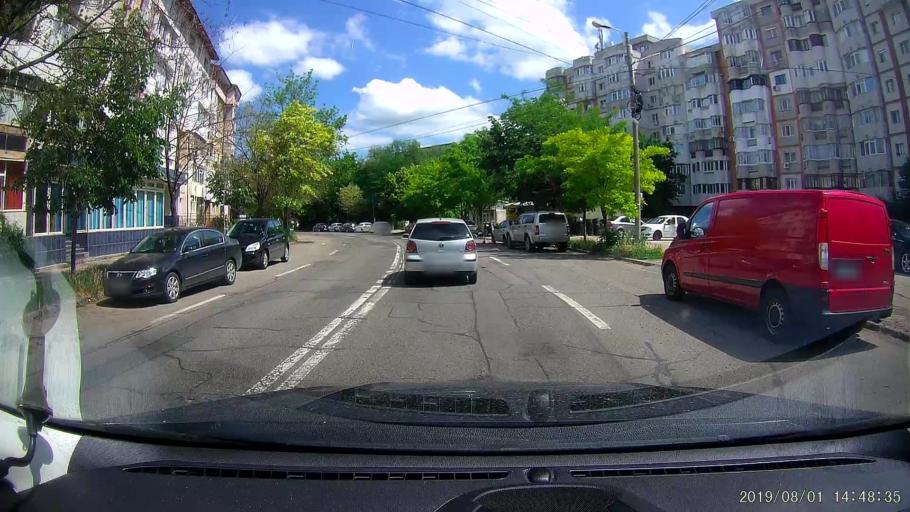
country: RO
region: Galati
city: Galati
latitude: 45.4096
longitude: 28.0101
